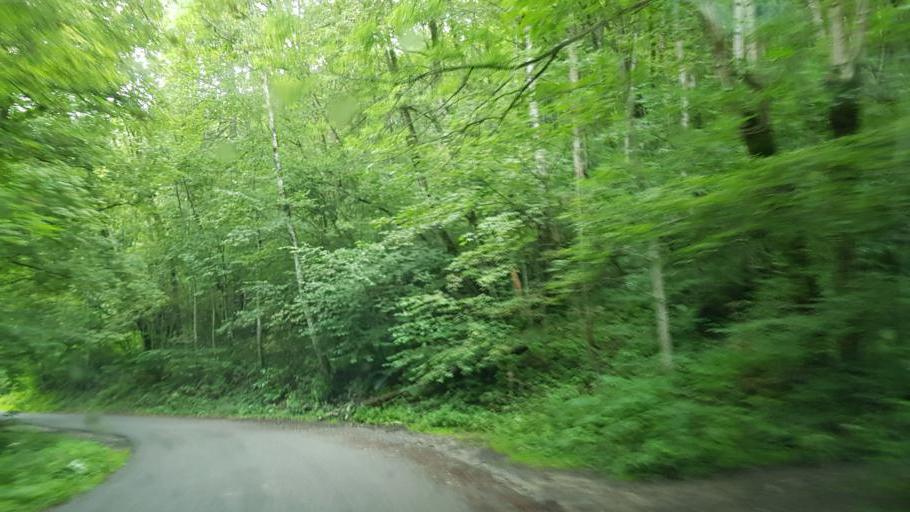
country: IT
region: Piedmont
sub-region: Provincia di Cuneo
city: Sampeyre
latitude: 44.5762
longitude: 7.1777
